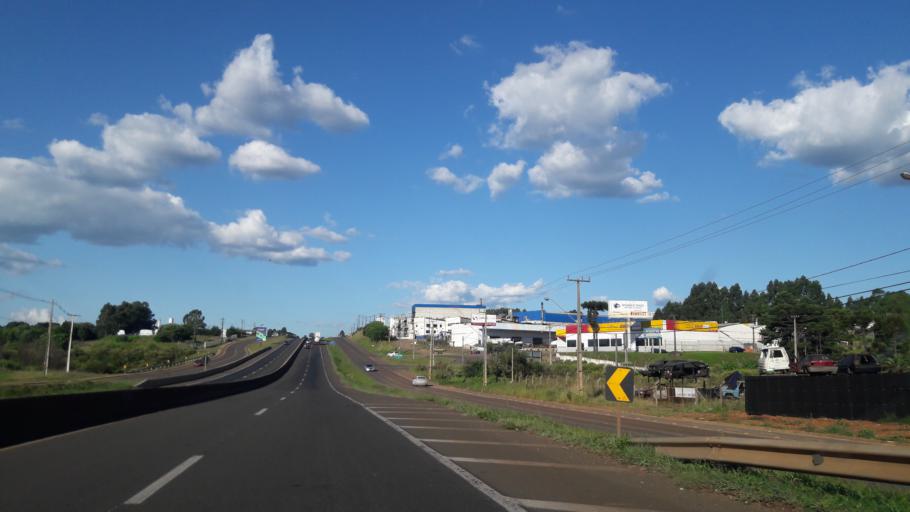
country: BR
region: Parana
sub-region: Guarapuava
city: Guarapuava
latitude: -25.3573
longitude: -51.4632
